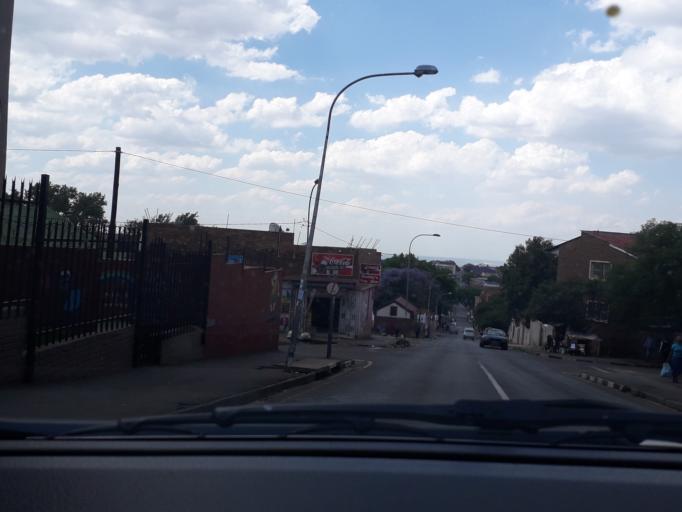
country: ZA
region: Gauteng
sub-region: City of Johannesburg Metropolitan Municipality
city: Johannesburg
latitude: -26.1837
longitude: 28.0671
